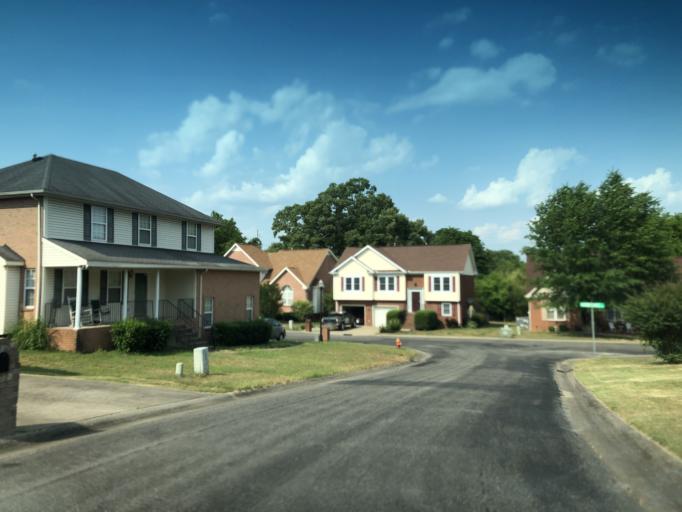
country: US
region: Tennessee
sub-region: Davidson County
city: Goodlettsville
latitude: 36.2627
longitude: -86.7233
